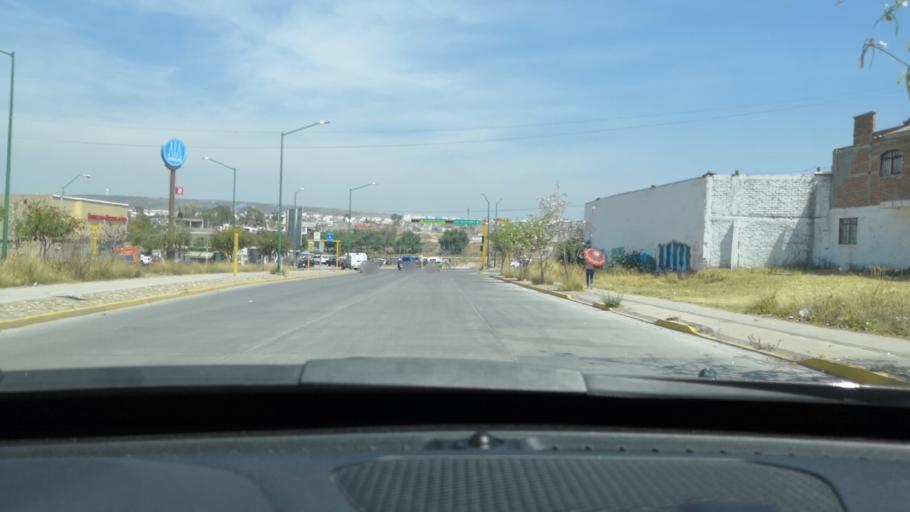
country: MX
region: Guanajuato
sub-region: Leon
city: Ejido la Joya
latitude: 21.1385
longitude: -101.7352
